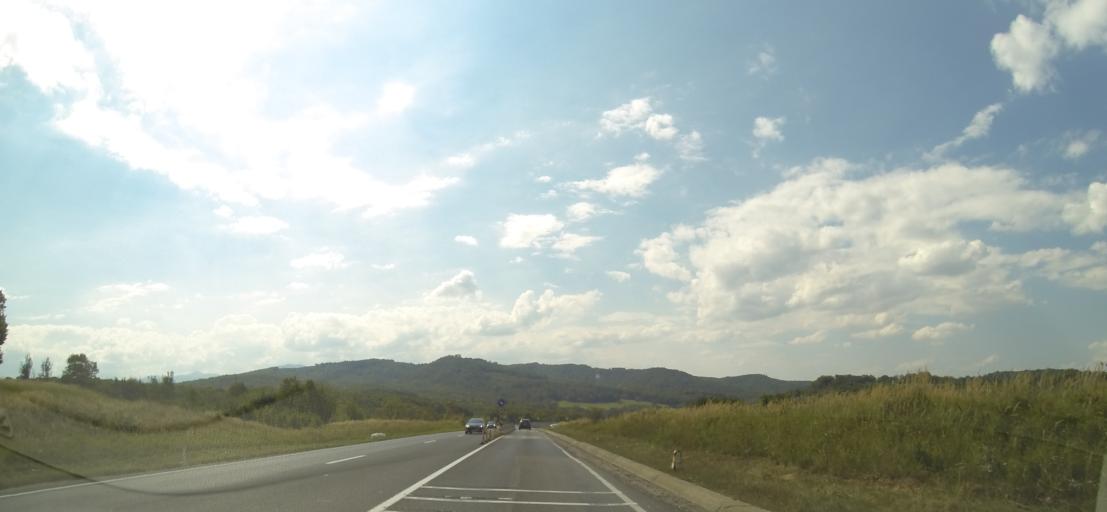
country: RO
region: Brasov
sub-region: Comuna Sinca Noua
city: Sinca Noua
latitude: 45.7535
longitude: 25.2770
